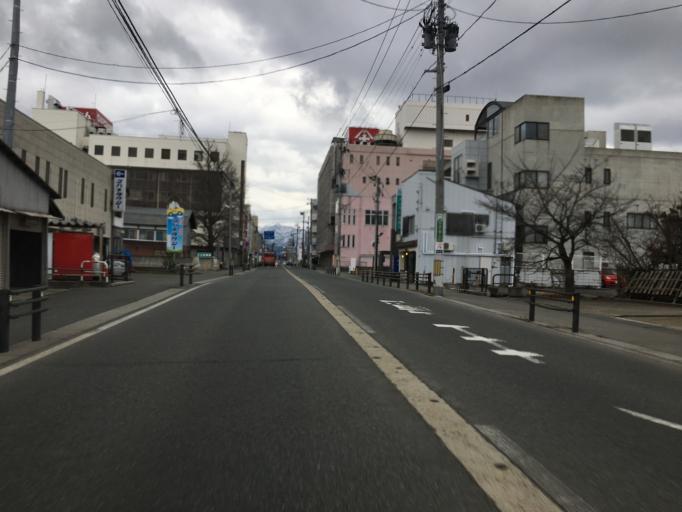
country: JP
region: Yamagata
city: Yonezawa
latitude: 37.9132
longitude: 140.1131
